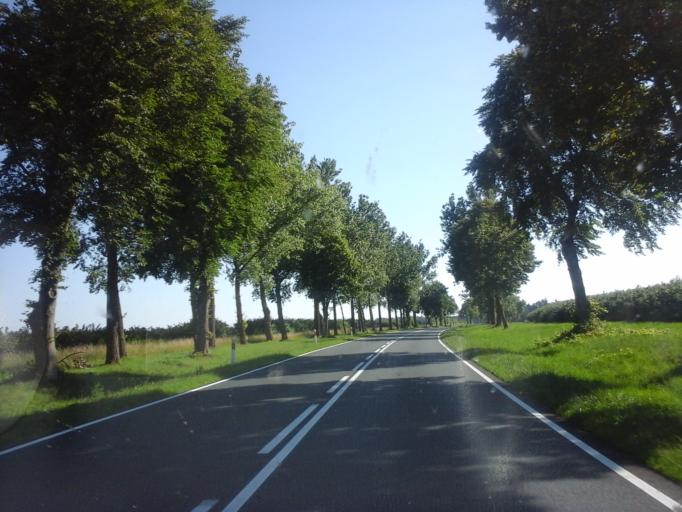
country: PL
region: West Pomeranian Voivodeship
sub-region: Powiat gryficki
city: Ploty
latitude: 53.7675
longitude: 15.2395
